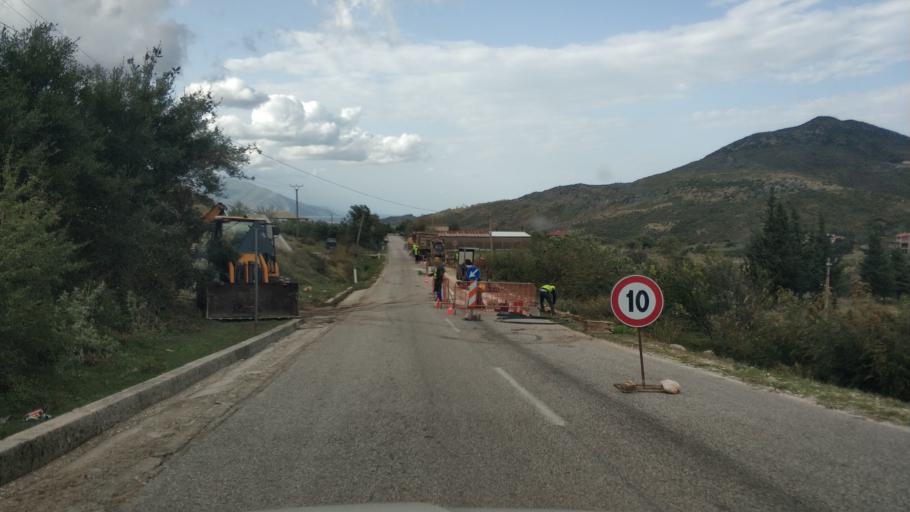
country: AL
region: Vlore
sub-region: Rrethi i Vlores
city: Orikum
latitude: 40.2688
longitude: 19.5150
